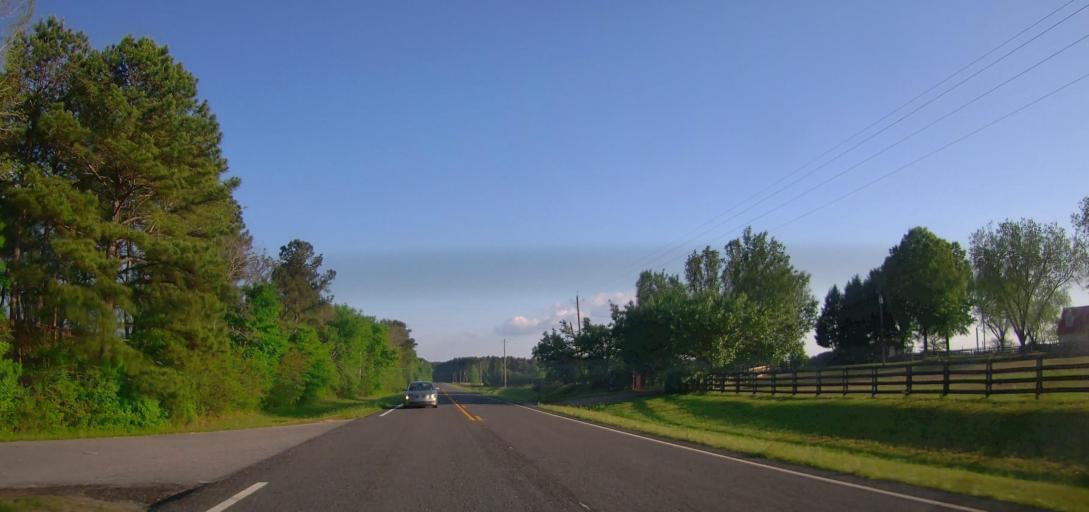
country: US
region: Georgia
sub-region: Jasper County
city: Monticello
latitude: 33.4376
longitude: -83.6200
